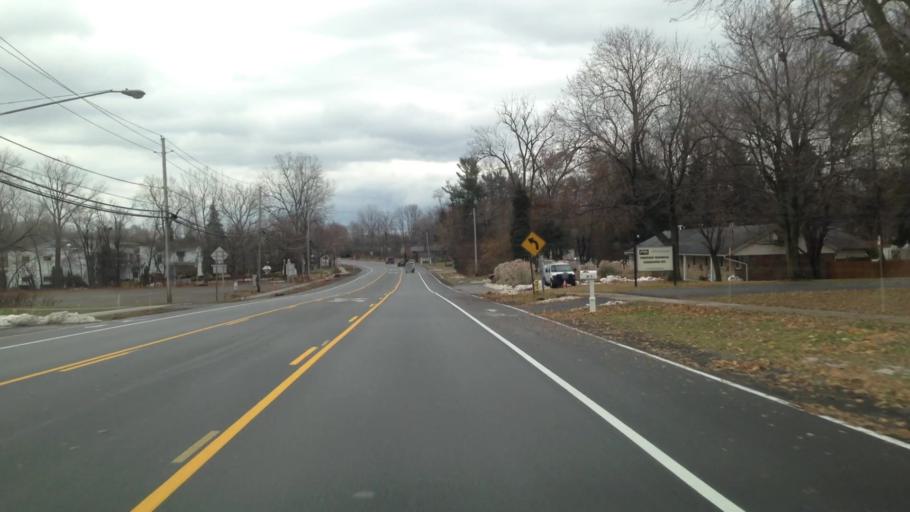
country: US
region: New York
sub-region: Erie County
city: Harris Hill
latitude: 42.9653
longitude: -78.6704
